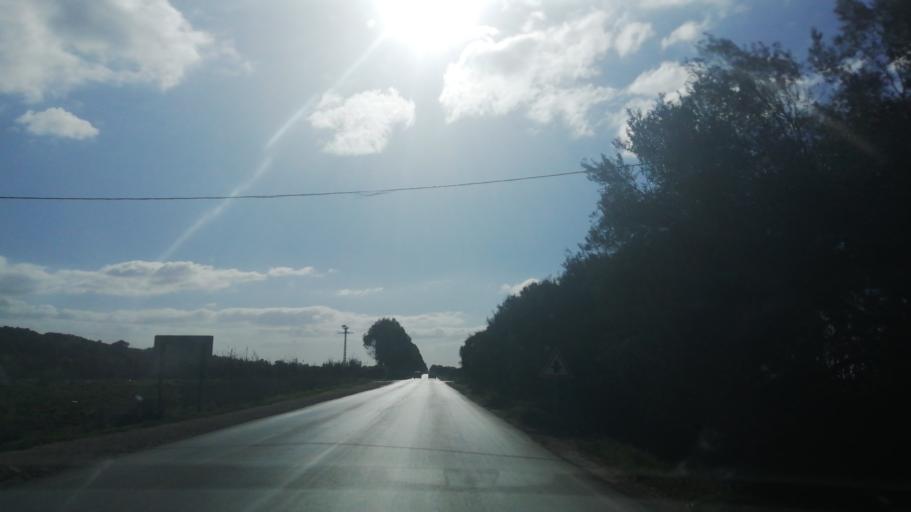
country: DZ
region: Mostaganem
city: Mostaganem
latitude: 35.9876
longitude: 0.2899
